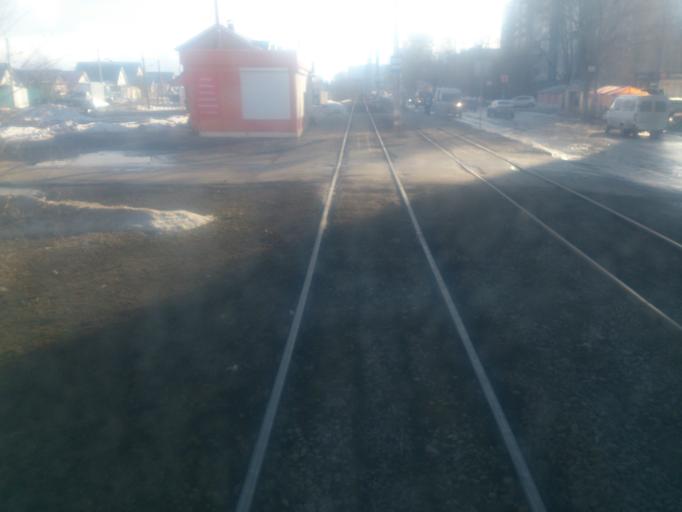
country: RU
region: Ulyanovsk
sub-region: Ulyanovskiy Rayon
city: Ulyanovsk
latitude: 54.2681
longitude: 48.2842
